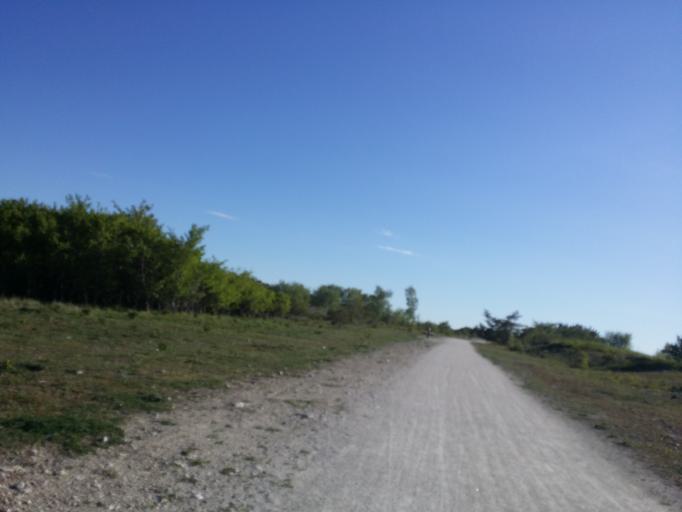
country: SE
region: Gotland
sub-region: Gotland
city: Vibble
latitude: 57.6217
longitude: 18.2684
